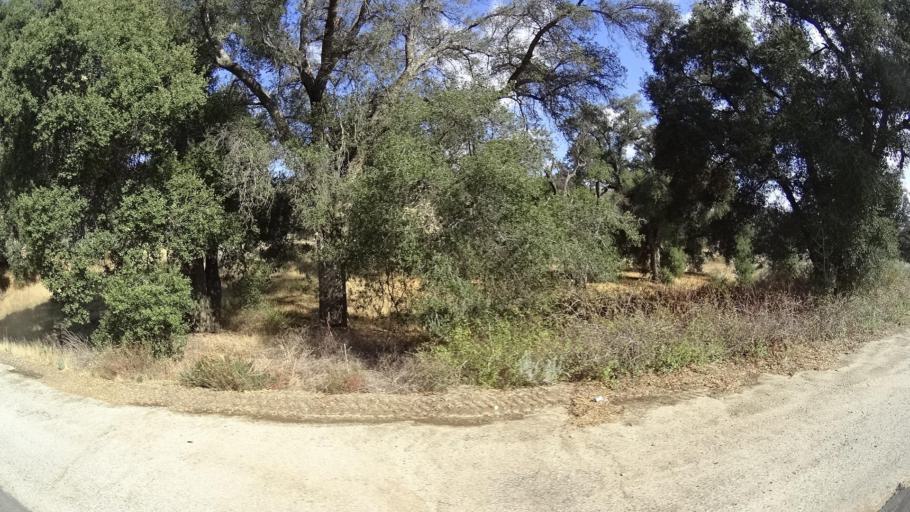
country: US
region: California
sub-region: San Diego County
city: Pine Valley
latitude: 32.7236
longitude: -116.4962
